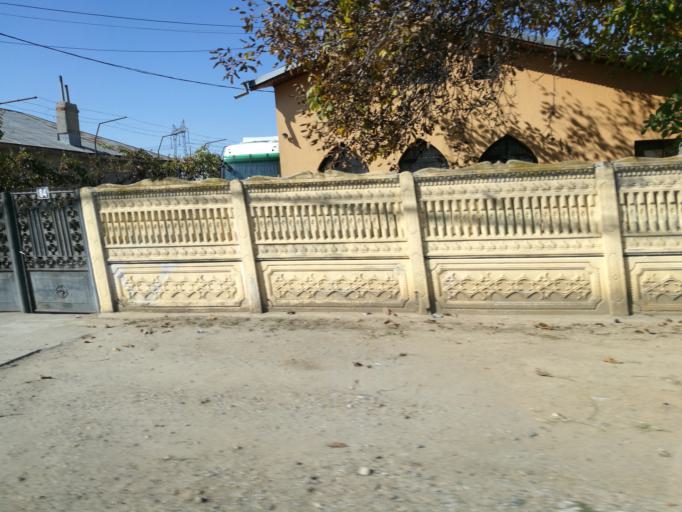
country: RO
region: Giurgiu
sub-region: Comuna Joita
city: Bacu
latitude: 44.4748
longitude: 25.8893
